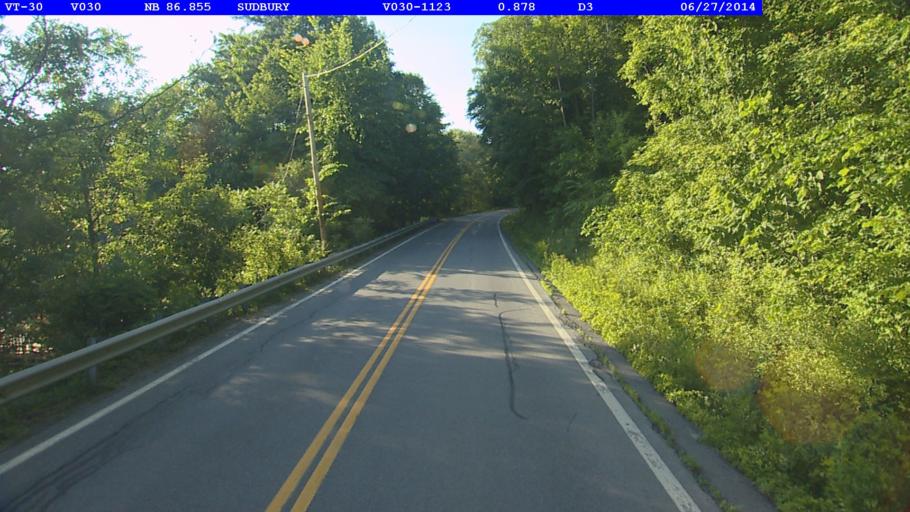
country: US
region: Vermont
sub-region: Rutland County
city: Brandon
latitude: 43.7619
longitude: -73.1960
